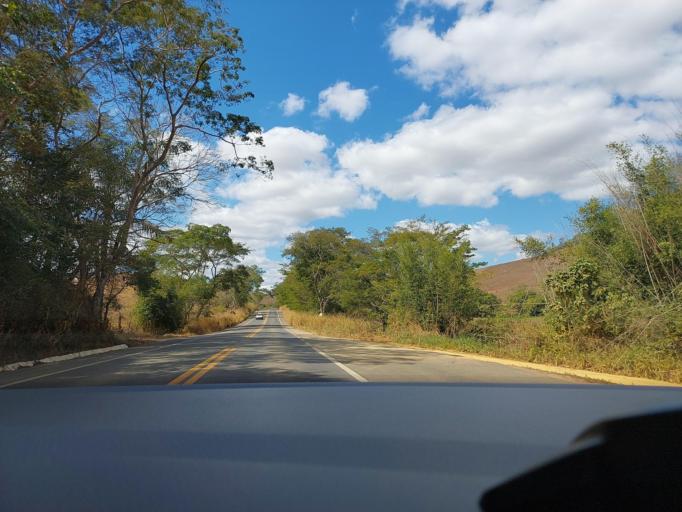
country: BR
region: Minas Gerais
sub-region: Muriae
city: Muriae
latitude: -21.1491
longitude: -42.1588
